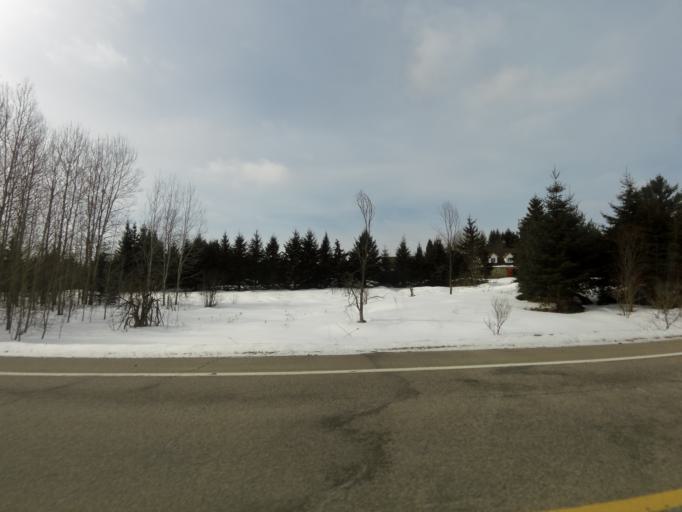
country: CA
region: Quebec
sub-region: Laurentides
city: Mont-Laurier
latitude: 46.4513
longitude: -75.5023
